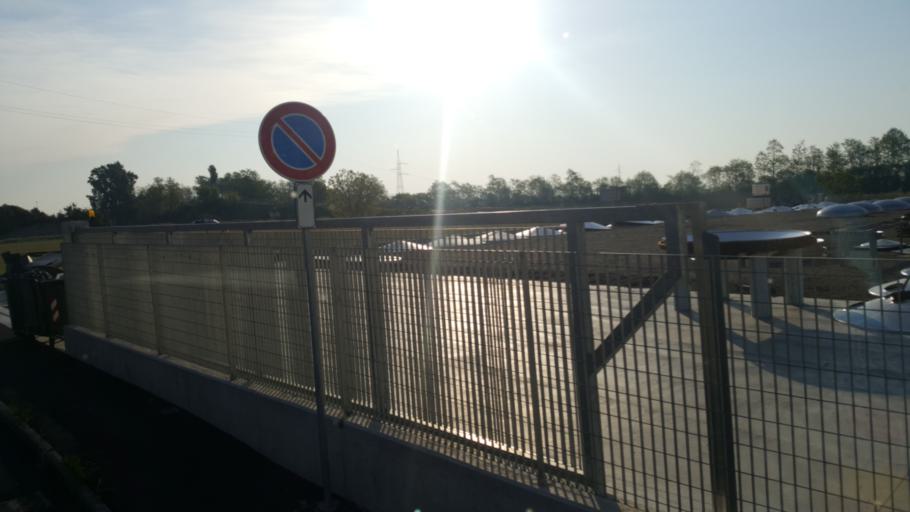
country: IT
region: Lombardy
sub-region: Provincia di Cremona
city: Santa Maria dei Sabbioni
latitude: 45.2407
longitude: 9.8406
